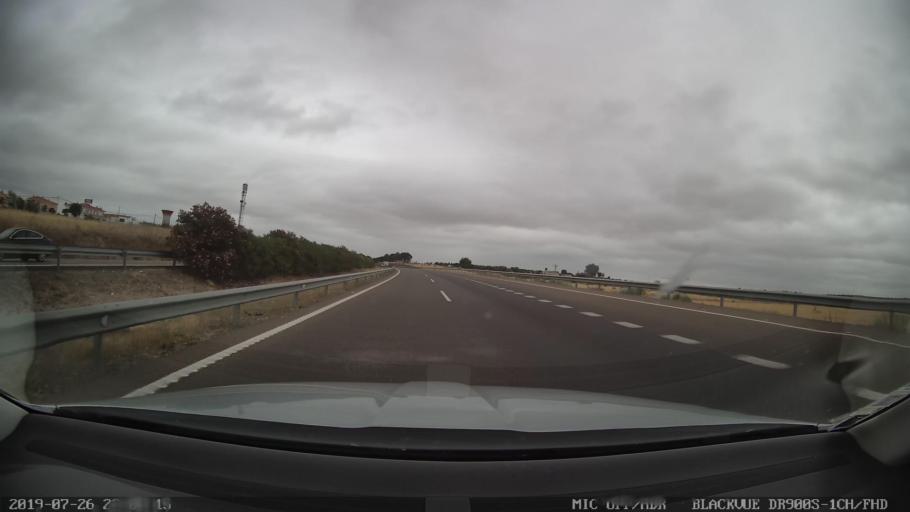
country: ES
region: Extremadura
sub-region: Provincia de Badajoz
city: Trujillanos
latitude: 38.9474
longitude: -6.2614
